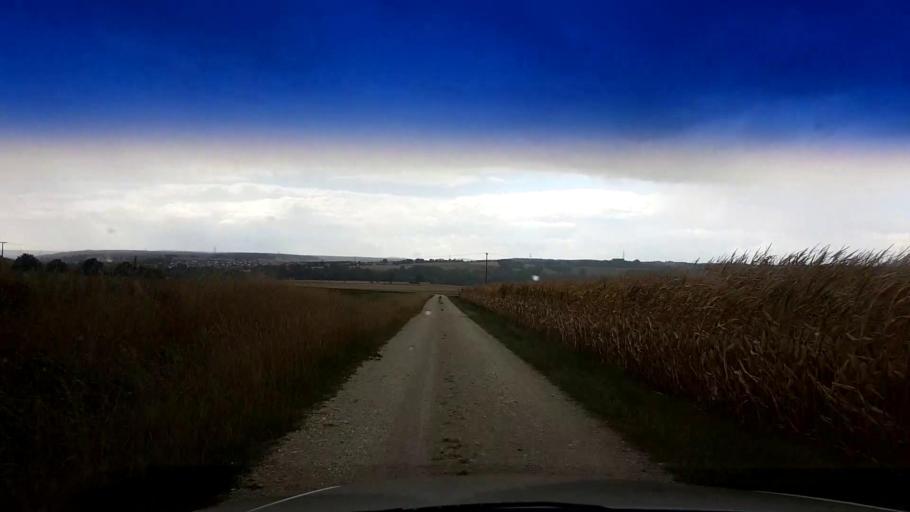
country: DE
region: Bavaria
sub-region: Upper Franconia
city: Litzendorf
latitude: 49.9459
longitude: 11.0082
